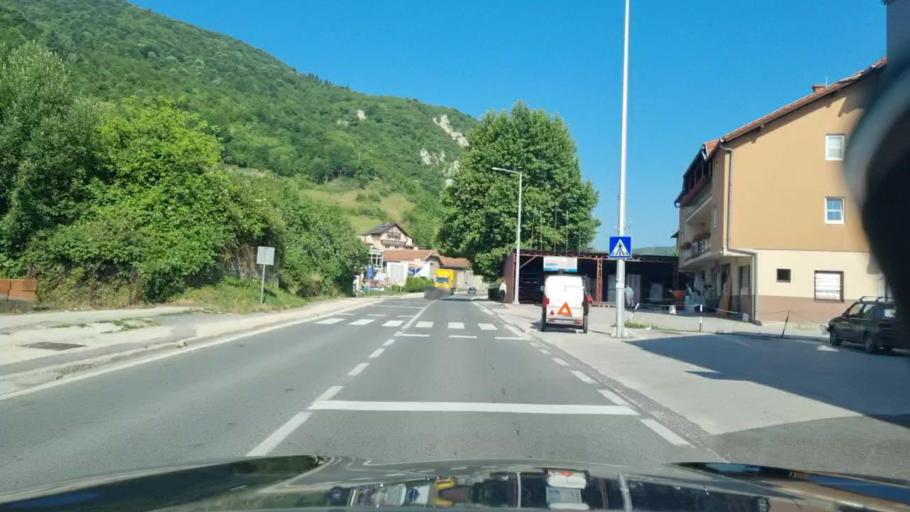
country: BA
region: Federation of Bosnia and Herzegovina
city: Jajce
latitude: 44.3391
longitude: 17.2651
